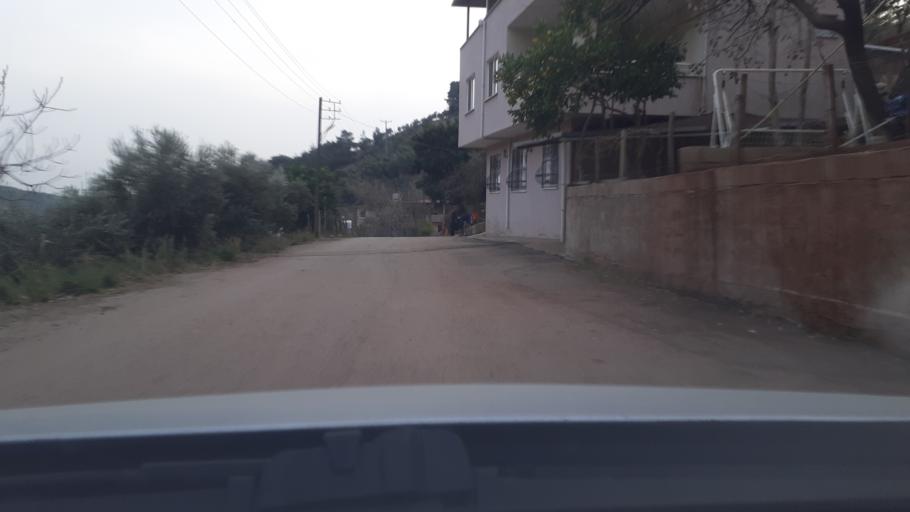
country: TR
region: Hatay
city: Kirikhan
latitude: 36.5342
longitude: 36.3146
